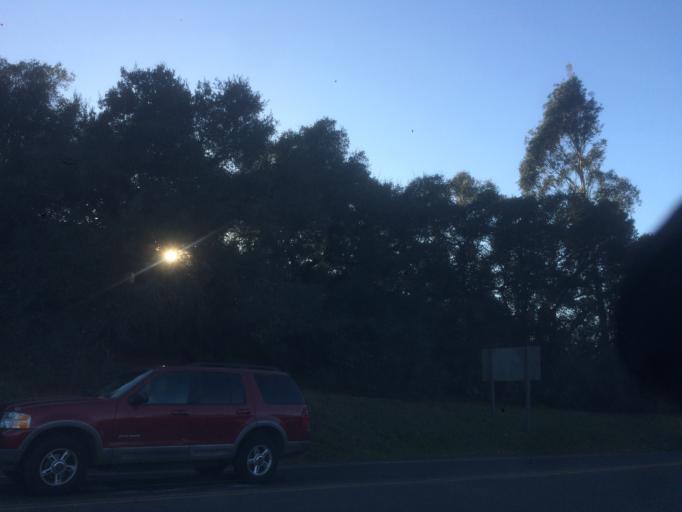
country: US
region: California
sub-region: Santa Barbara County
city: Mission Canyon
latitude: 34.4364
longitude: -119.7540
